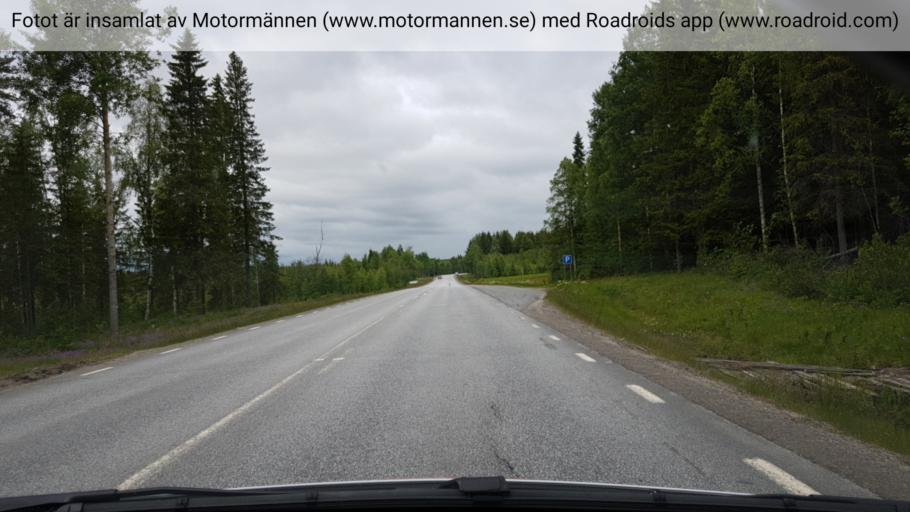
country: SE
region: Vaesterbotten
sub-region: Vannas Kommun
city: Vaennaes
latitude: 63.9293
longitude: 19.7734
